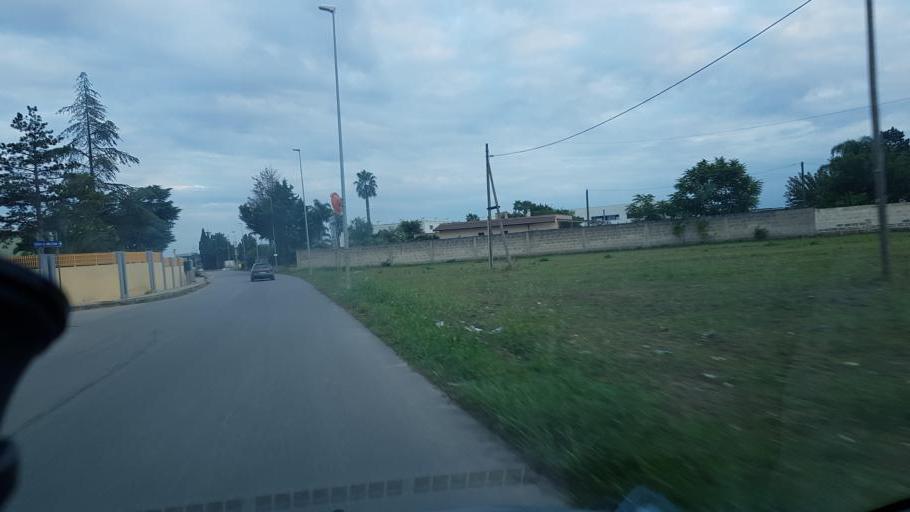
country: IT
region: Apulia
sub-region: Provincia di Brindisi
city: Latiano
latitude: 40.5475
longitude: 17.7269
